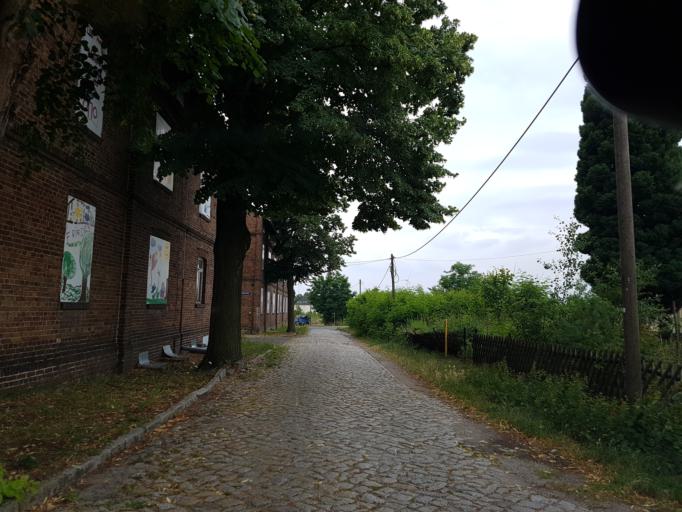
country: DE
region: Brandenburg
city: Schipkau
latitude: 51.5631
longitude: 13.8908
